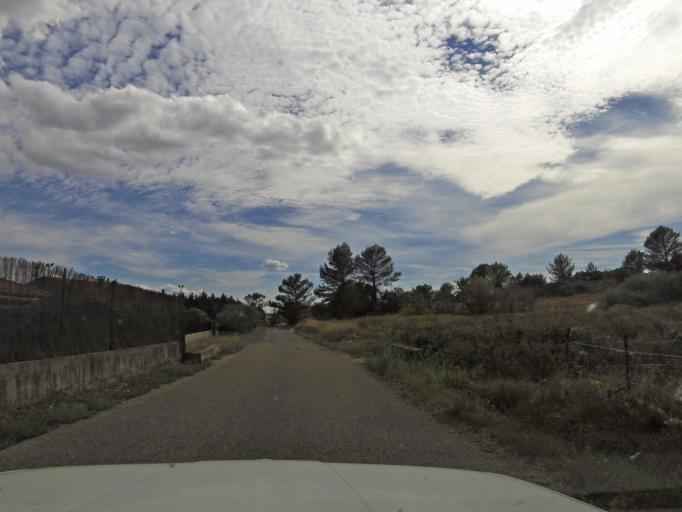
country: FR
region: Languedoc-Roussillon
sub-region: Departement du Gard
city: Bagard
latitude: 44.0767
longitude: 4.0551
